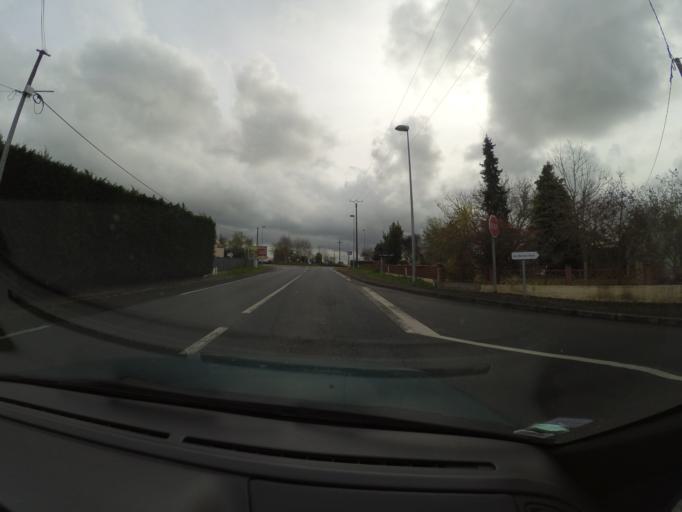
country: FR
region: Pays de la Loire
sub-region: Departement de la Loire-Atlantique
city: La Remaudiere
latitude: 47.2400
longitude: -1.2142
